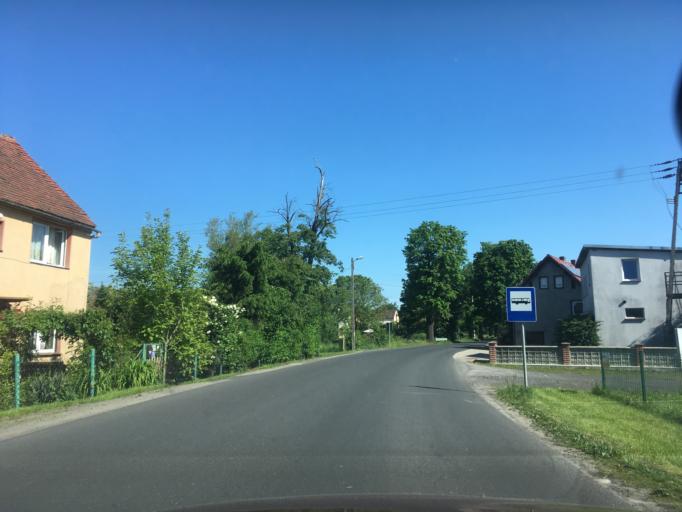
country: PL
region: Lower Silesian Voivodeship
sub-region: Powiat zgorzelecki
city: Sulikow
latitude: 51.0830
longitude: 15.0561
